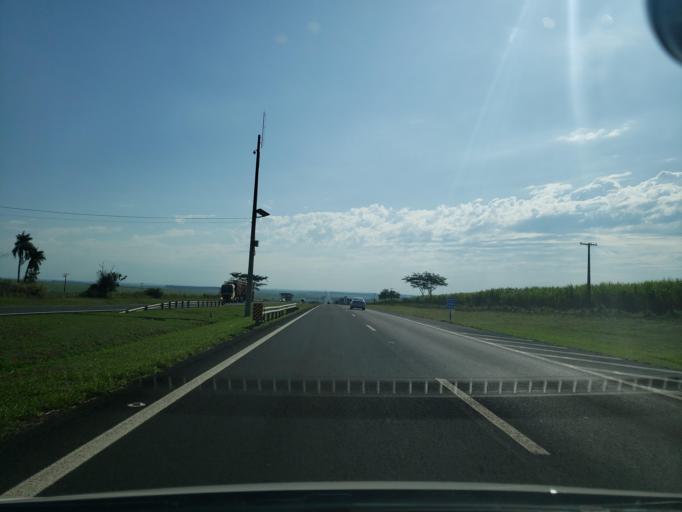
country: BR
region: Sao Paulo
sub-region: Penapolis
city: Penapolis
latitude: -21.5097
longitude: -50.0198
